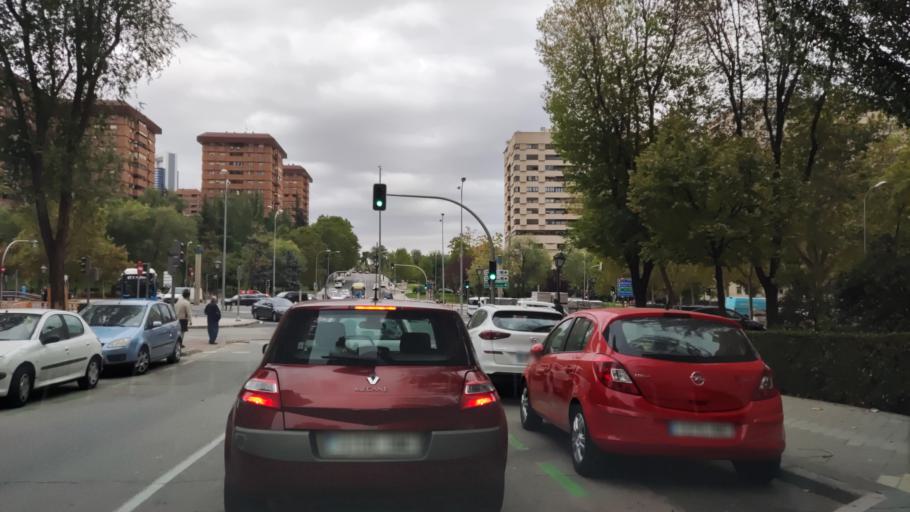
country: ES
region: Madrid
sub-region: Provincia de Madrid
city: Tetuan de las Victorias
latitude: 40.4844
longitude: -3.7001
